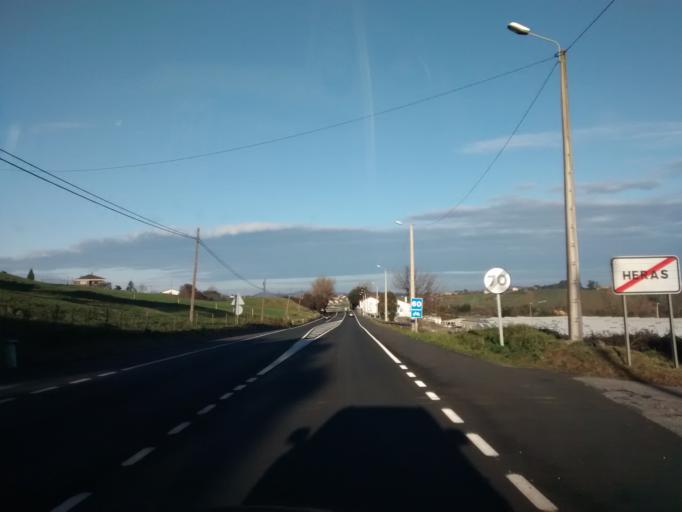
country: ES
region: Cantabria
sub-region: Provincia de Cantabria
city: El Astillero
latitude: 43.3970
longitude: -3.7706
